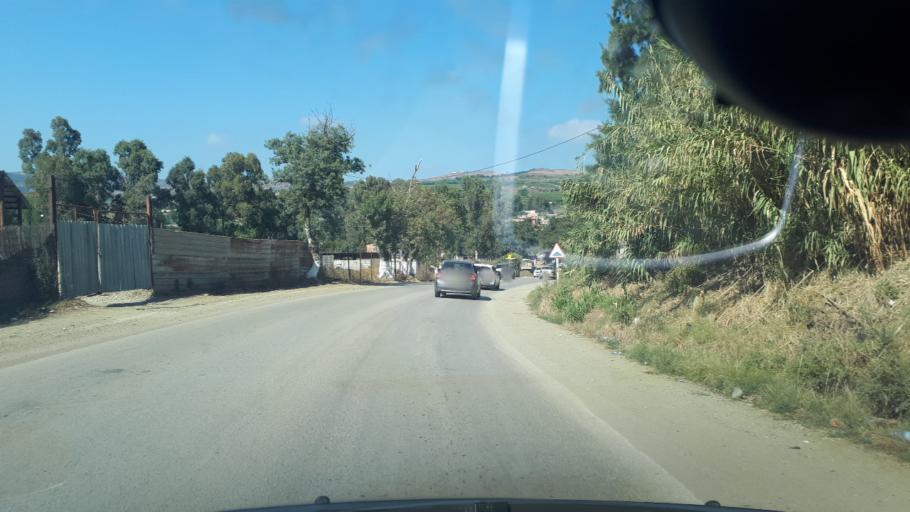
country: DZ
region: Boumerdes
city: Dellys
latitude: 36.8645
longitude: 3.8787
